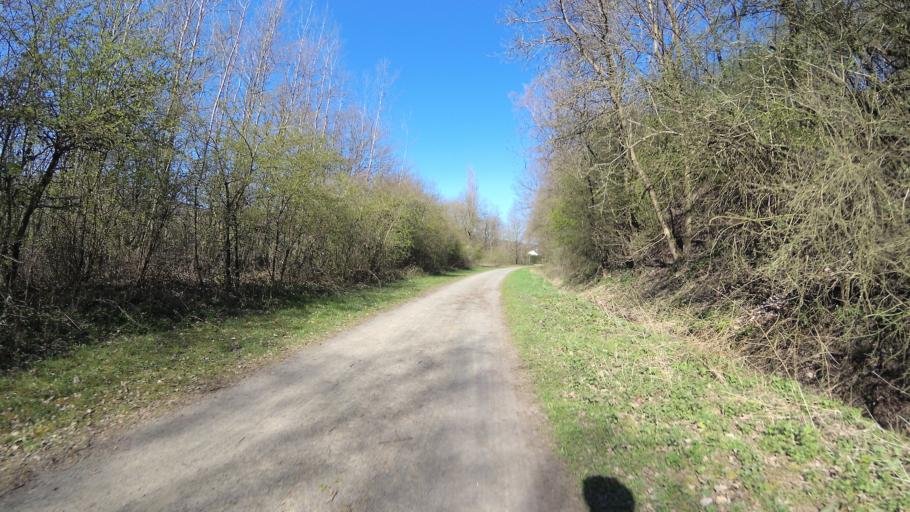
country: DE
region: Rheinland-Pfalz
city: Thallichtenberg
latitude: 49.5509
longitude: 7.3452
